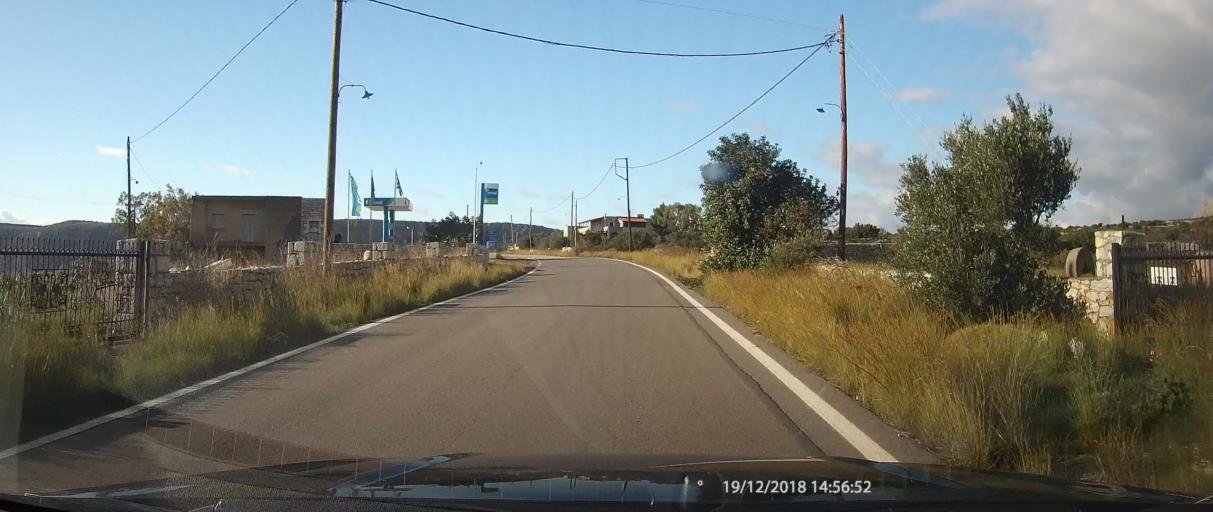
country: GR
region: Peloponnese
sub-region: Nomos Lakonias
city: Gytheio
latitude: 36.4787
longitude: 22.4123
